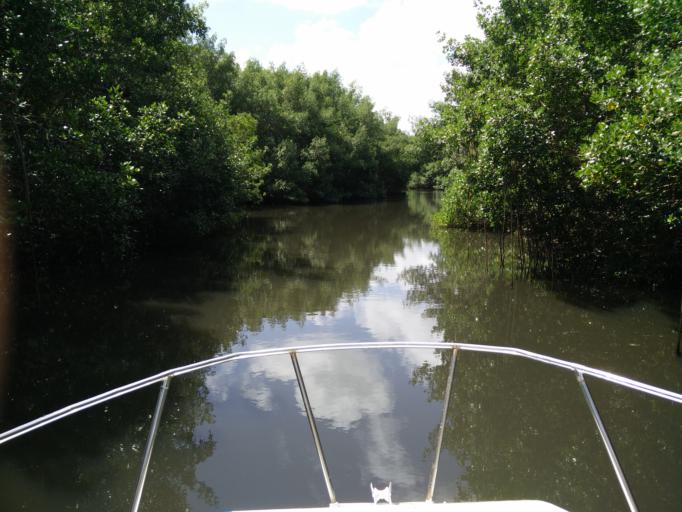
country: GP
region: Guadeloupe
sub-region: Guadeloupe
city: Petit-Canal
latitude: 16.3501
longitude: -61.4885
